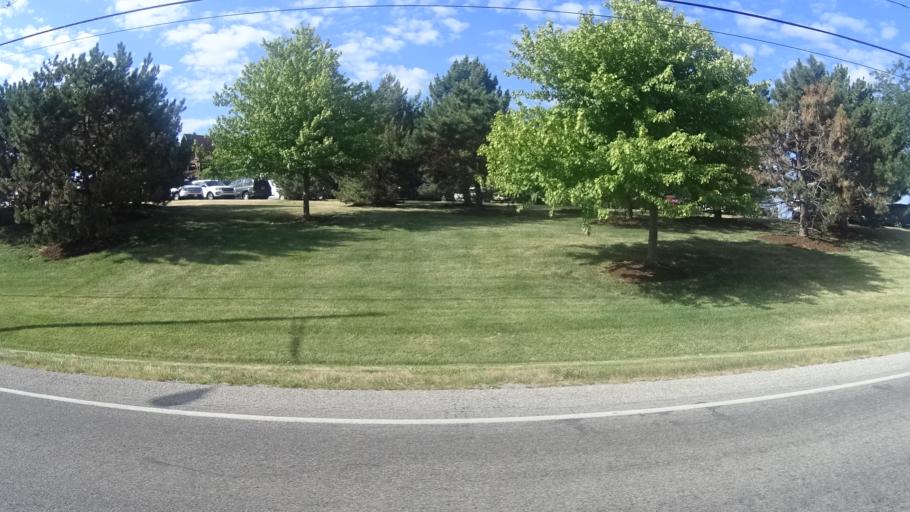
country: US
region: Ohio
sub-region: Erie County
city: Sandusky
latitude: 41.4144
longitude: -82.6662
